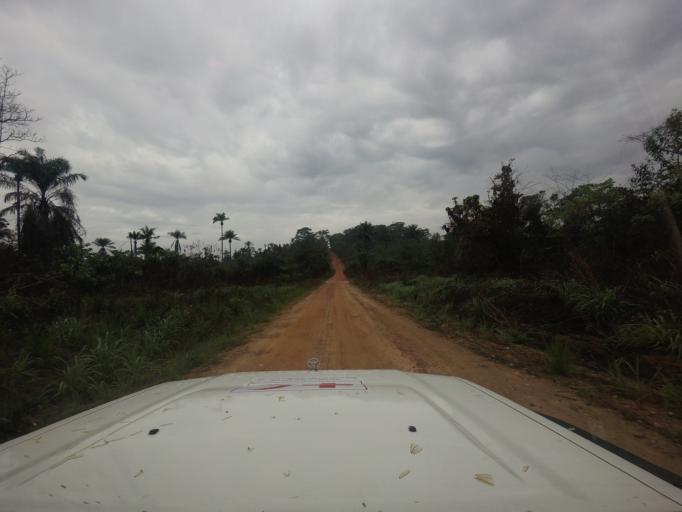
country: LR
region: Lofa
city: Voinjama
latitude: 8.3752
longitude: -9.8629
